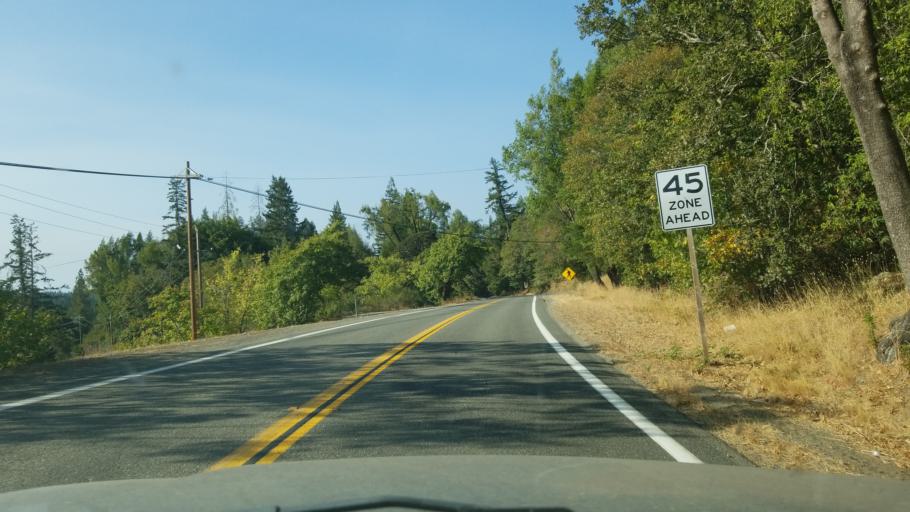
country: US
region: California
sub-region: Humboldt County
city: Redway
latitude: 40.2058
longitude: -123.7854
